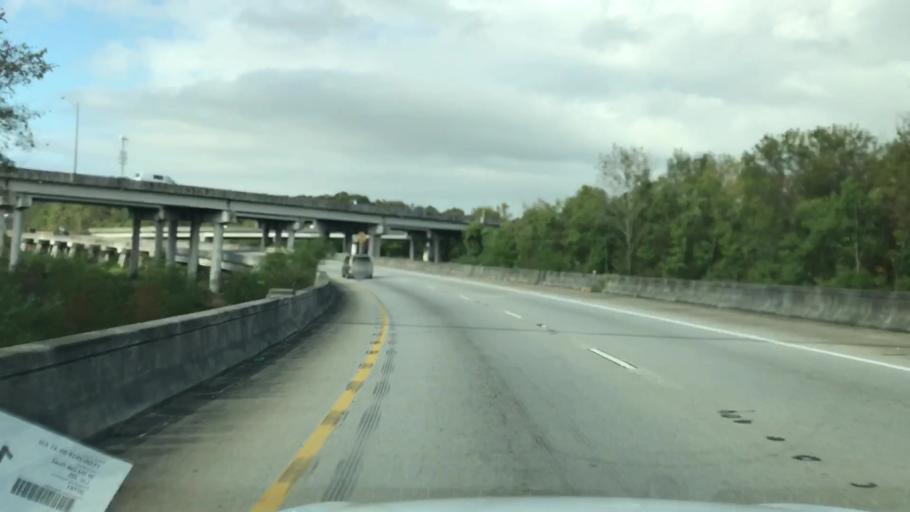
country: US
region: South Carolina
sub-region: Berkeley County
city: Hanahan
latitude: 32.8834
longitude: -80.0177
